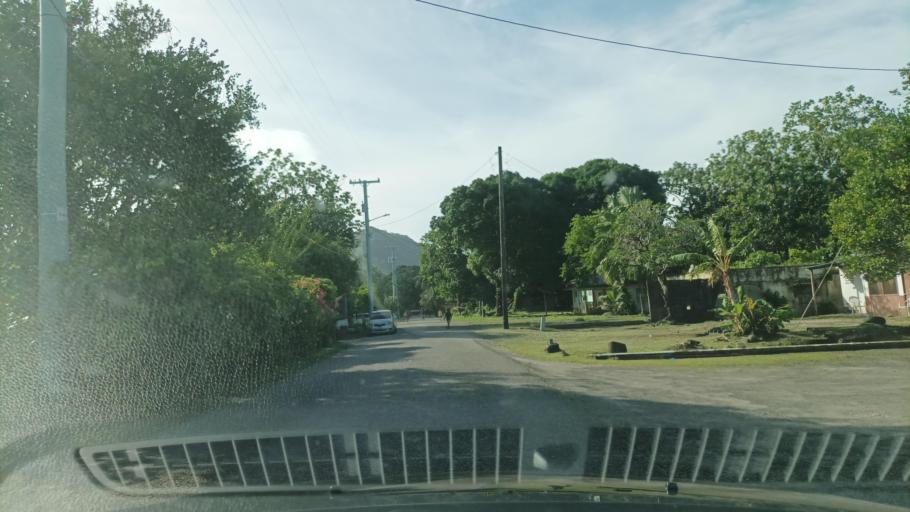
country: FM
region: Kosrae
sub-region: Lelu Municipality
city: Lelu
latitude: 5.3307
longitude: 163.0244
